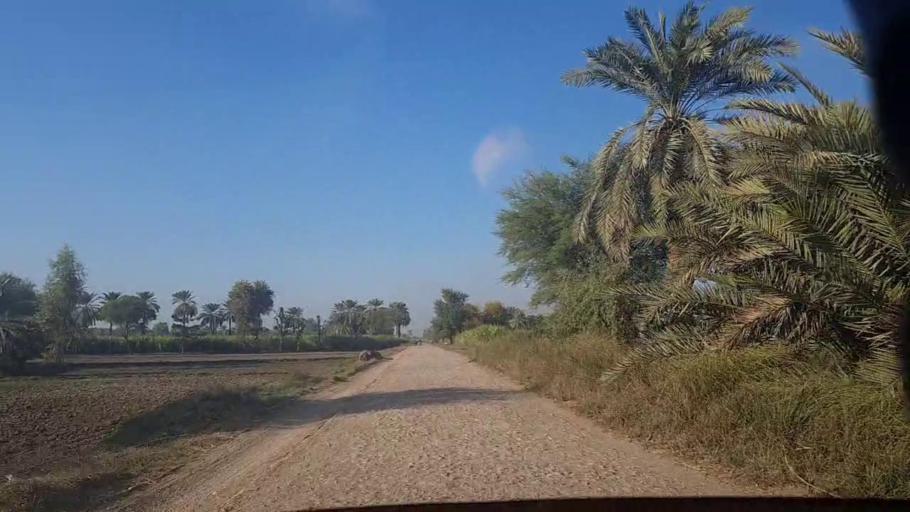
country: PK
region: Sindh
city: Sobhadero
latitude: 27.3934
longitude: 68.4201
